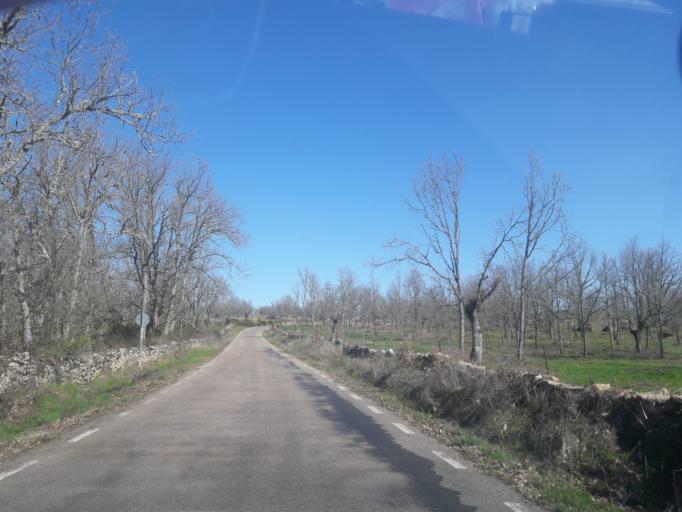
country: ES
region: Castille and Leon
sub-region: Provincia de Salamanca
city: Valsalabroso
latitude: 41.1100
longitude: -6.4831
